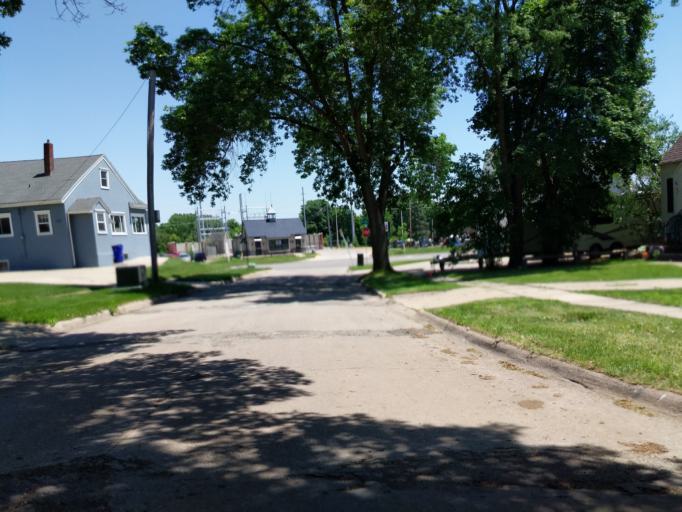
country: US
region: Iowa
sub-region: Linn County
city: Cedar Rapids
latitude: 42.0177
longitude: -91.6351
